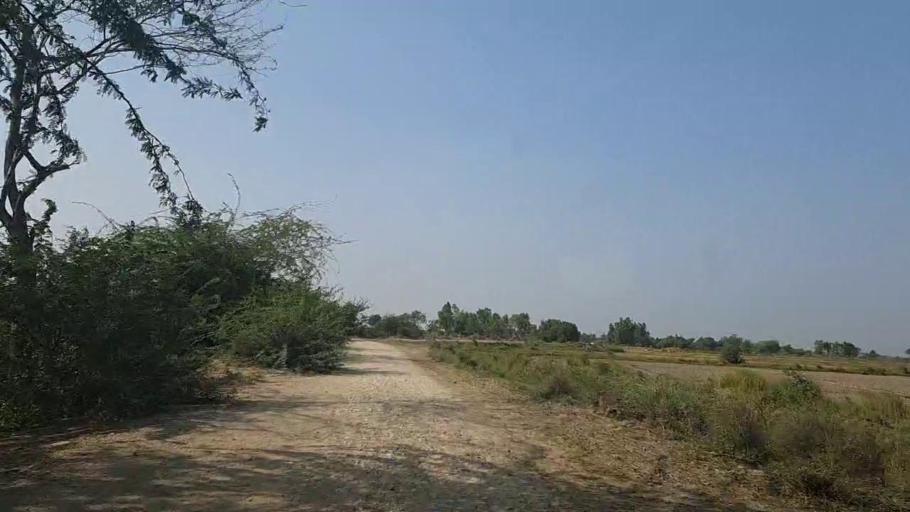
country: PK
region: Sindh
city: Mirpur Sakro
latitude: 24.5642
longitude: 67.8284
